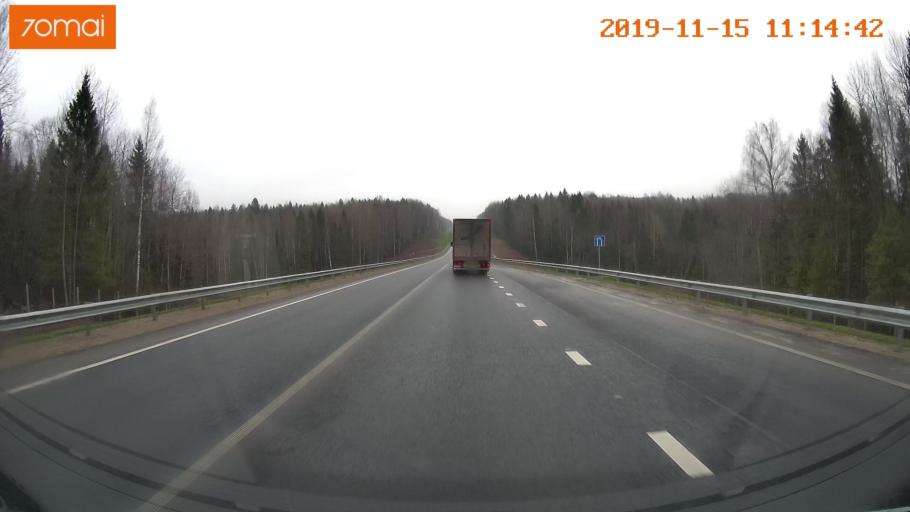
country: RU
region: Vologda
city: Chebsara
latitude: 59.1257
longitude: 39.1938
